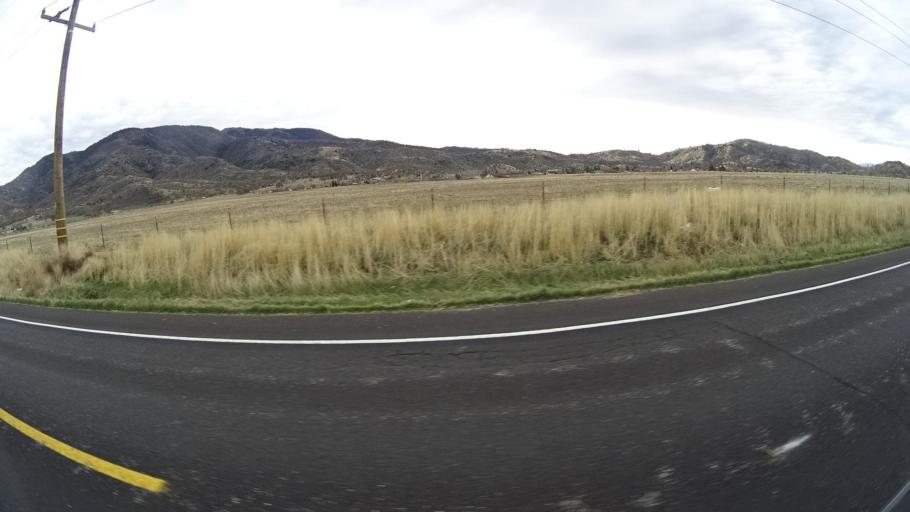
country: US
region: California
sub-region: Kern County
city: Stallion Springs
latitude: 35.0950
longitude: -118.6189
